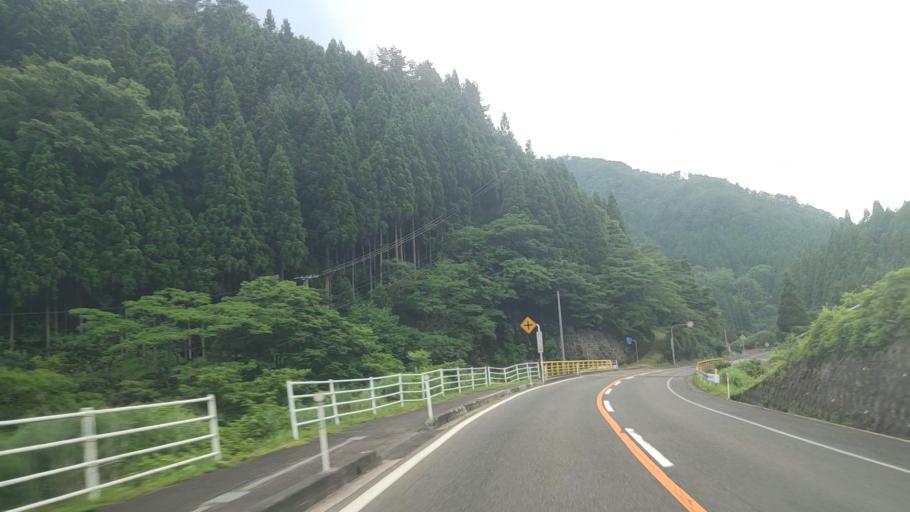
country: JP
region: Tottori
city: Kurayoshi
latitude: 35.3156
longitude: 133.8860
